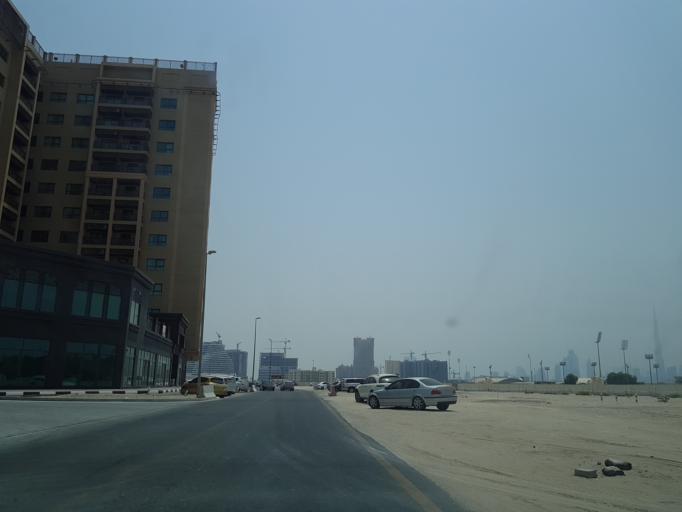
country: AE
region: Ash Shariqah
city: Sharjah
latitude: 25.2215
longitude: 55.3226
